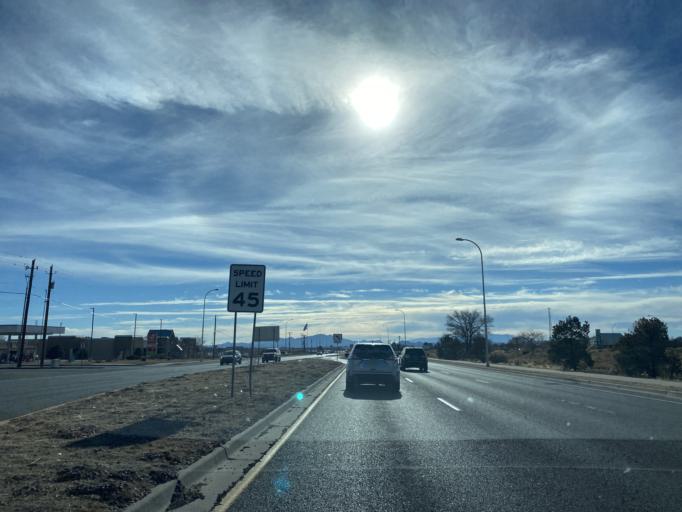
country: US
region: New Mexico
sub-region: Santa Fe County
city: Agua Fria
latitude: 35.6343
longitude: -106.0203
